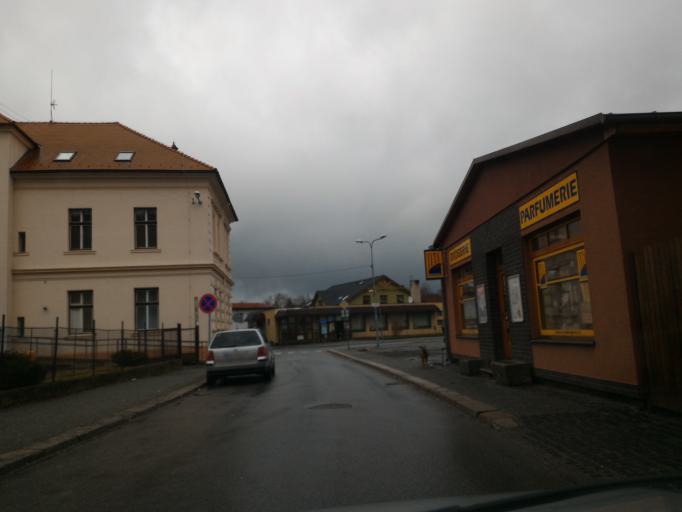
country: CZ
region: Liberecky
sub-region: Okres Liberec
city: Frydlant
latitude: 50.9225
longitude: 15.0800
